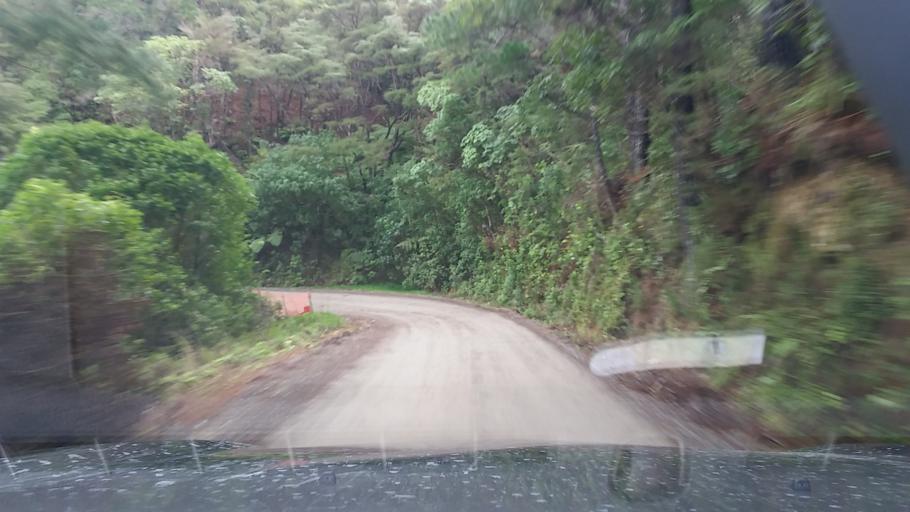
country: NZ
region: Marlborough
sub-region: Marlborough District
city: Picton
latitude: -41.1677
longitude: 174.0181
